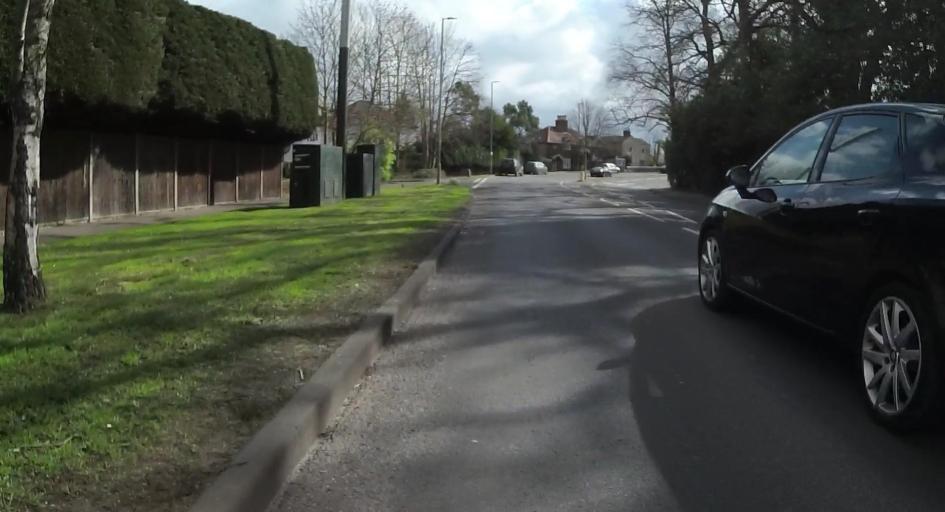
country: GB
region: England
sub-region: Surrey
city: West Byfleet
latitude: 51.3373
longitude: -0.5140
